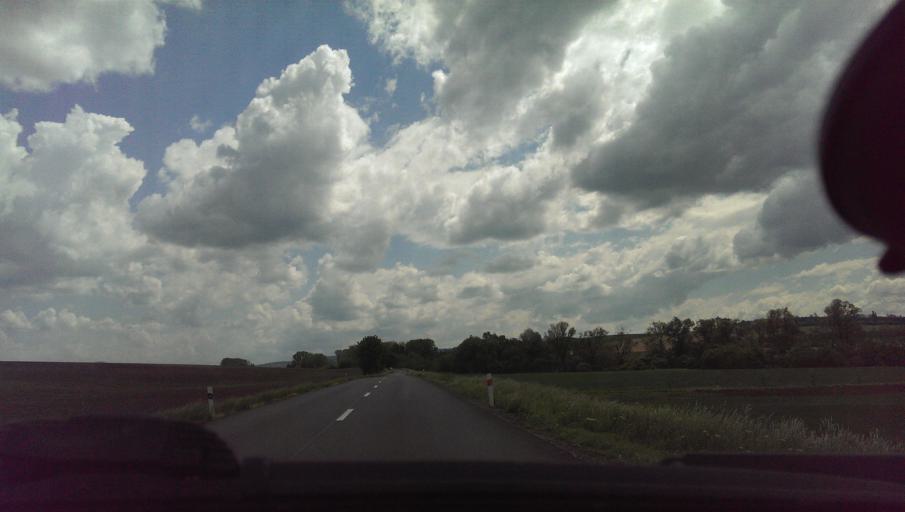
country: CZ
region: Zlin
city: Dolni Nemci
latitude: 48.9748
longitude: 17.5585
